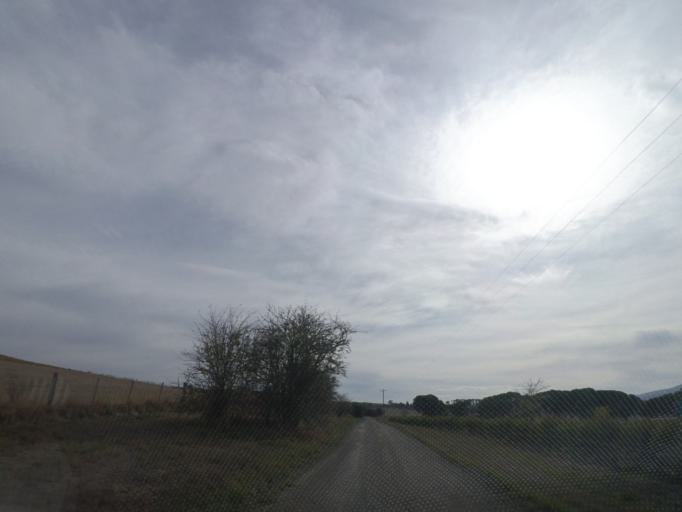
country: AU
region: Victoria
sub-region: Yarra Ranges
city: Yarra Glen
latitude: -37.6508
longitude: 145.4217
